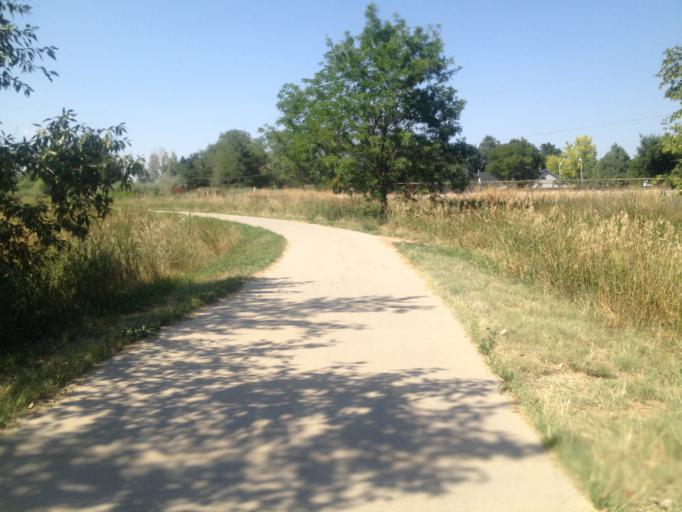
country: US
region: Colorado
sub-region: Boulder County
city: Louisville
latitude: 39.9973
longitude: -105.1402
